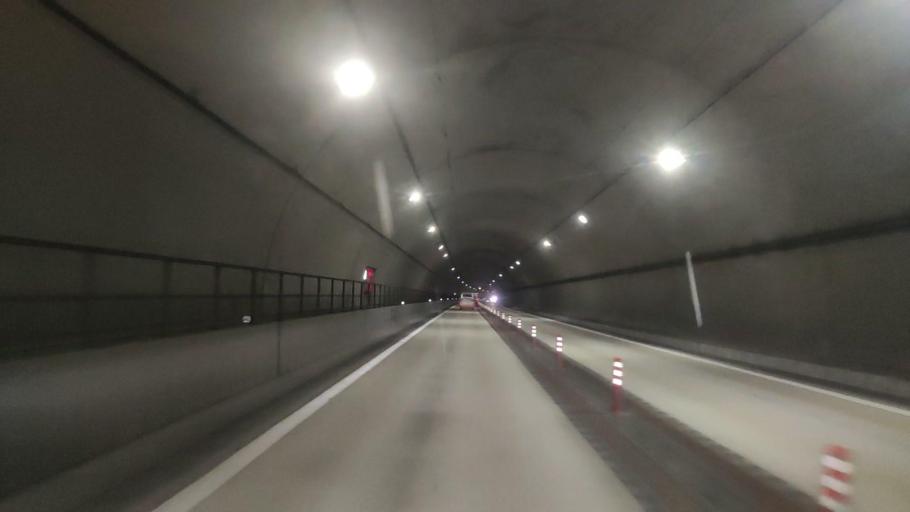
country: JP
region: Wakayama
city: Tanabe
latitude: 33.5873
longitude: 135.4449
